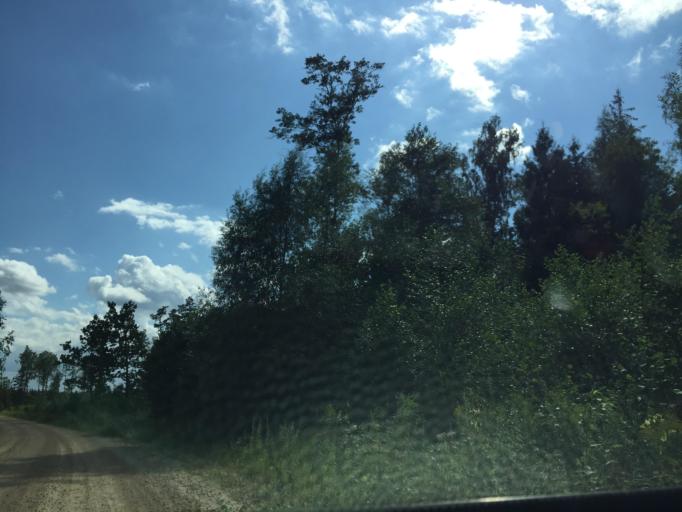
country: LV
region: Kegums
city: Kegums
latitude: 56.8236
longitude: 24.7465
